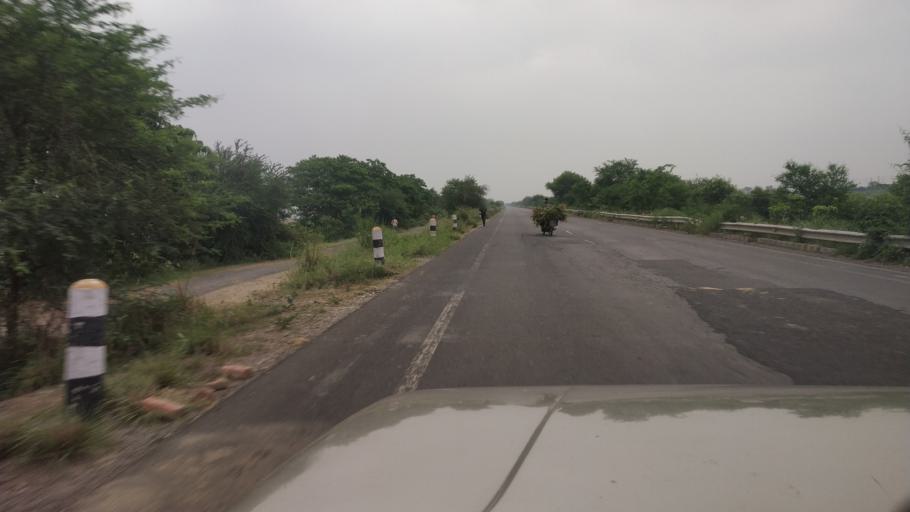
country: IN
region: Bihar
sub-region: Bhagalpur
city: Bhagalpur
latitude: 25.4040
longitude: 86.7910
